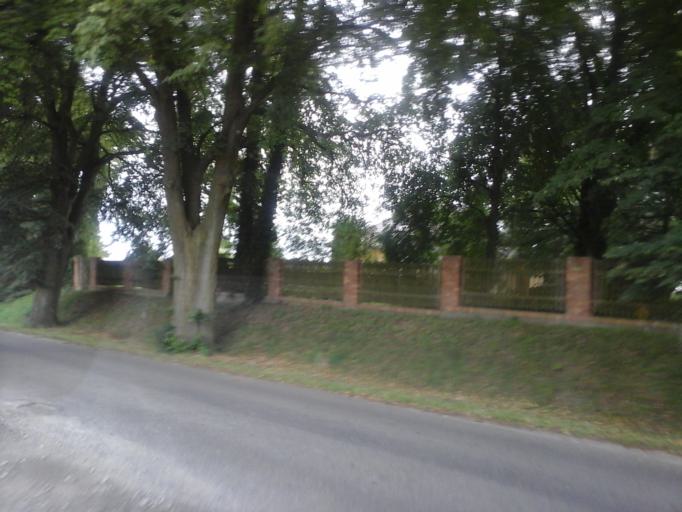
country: PL
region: West Pomeranian Voivodeship
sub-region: Powiat choszczenski
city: Recz
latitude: 53.2577
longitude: 15.5565
